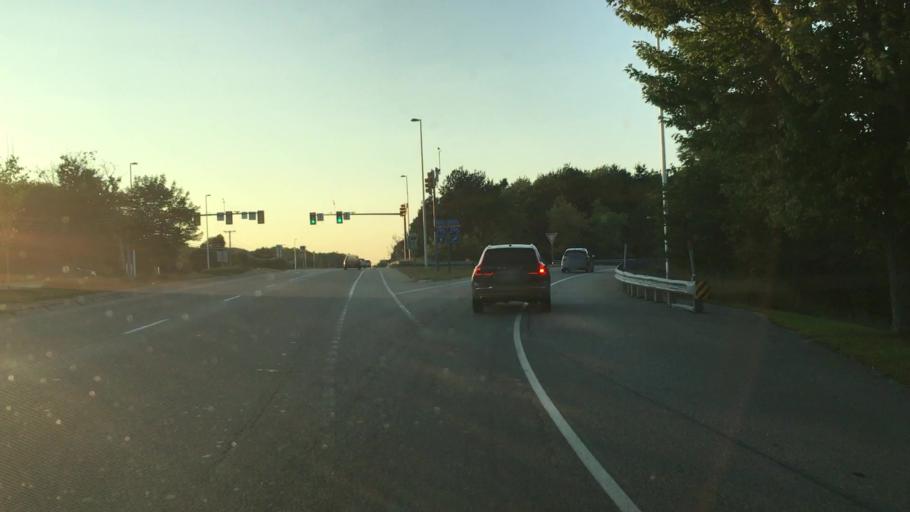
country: US
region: Maine
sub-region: Sagadahoc County
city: Topsham
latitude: 43.9407
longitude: -69.9767
